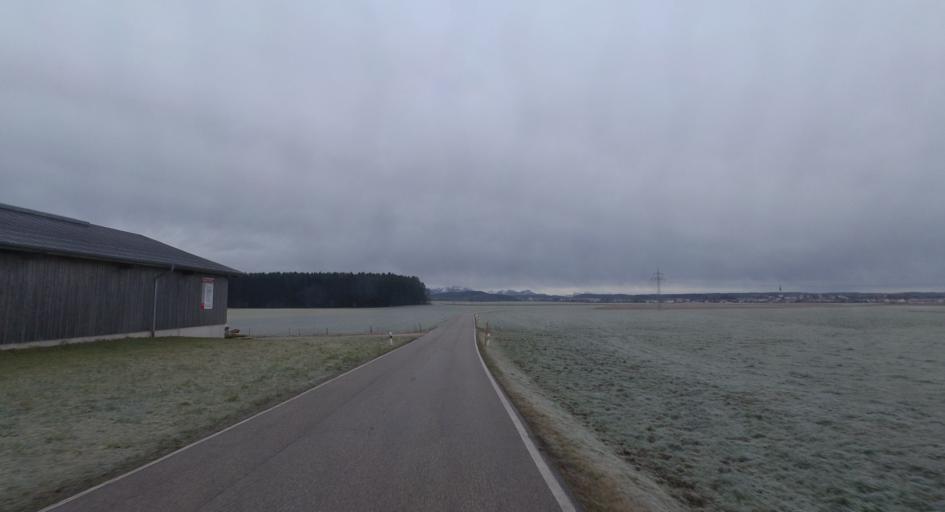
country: DE
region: Bavaria
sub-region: Upper Bavaria
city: Traunreut
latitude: 47.9417
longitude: 12.6274
